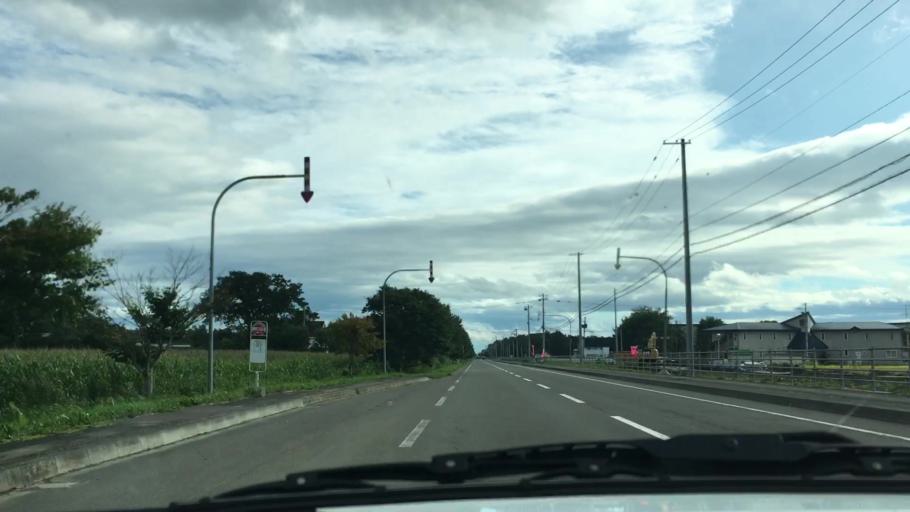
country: JP
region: Hokkaido
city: Otofuke
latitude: 43.2542
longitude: 143.2999
